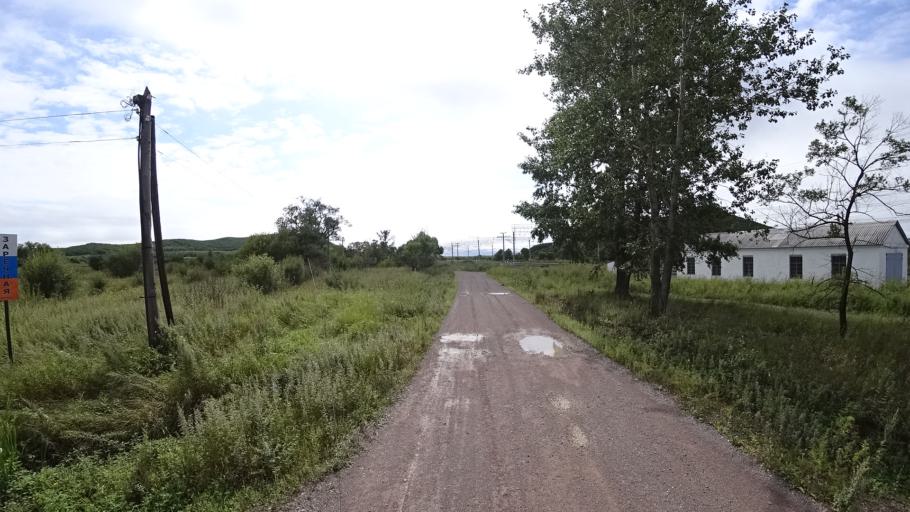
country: RU
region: Primorskiy
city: Lyalichi
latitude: 44.1383
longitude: 132.3740
